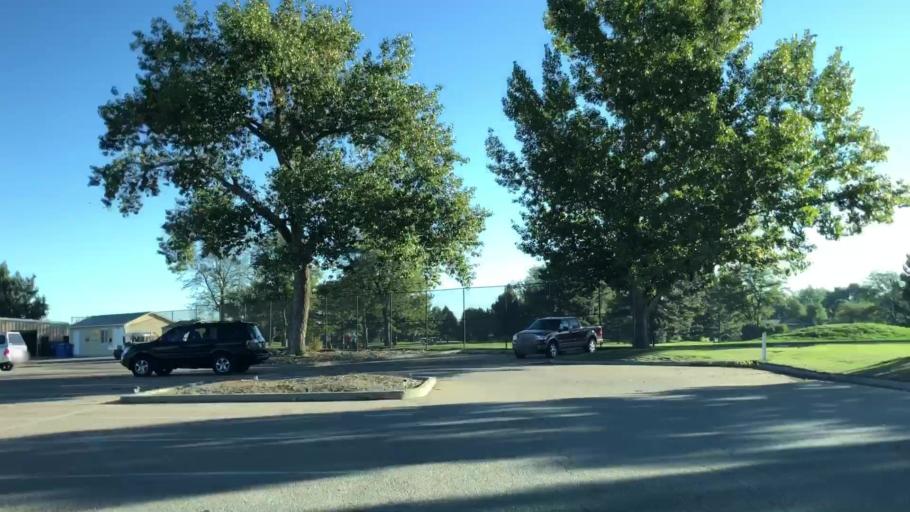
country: US
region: Colorado
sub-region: Larimer County
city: Loveland
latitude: 40.4240
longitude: -105.1056
